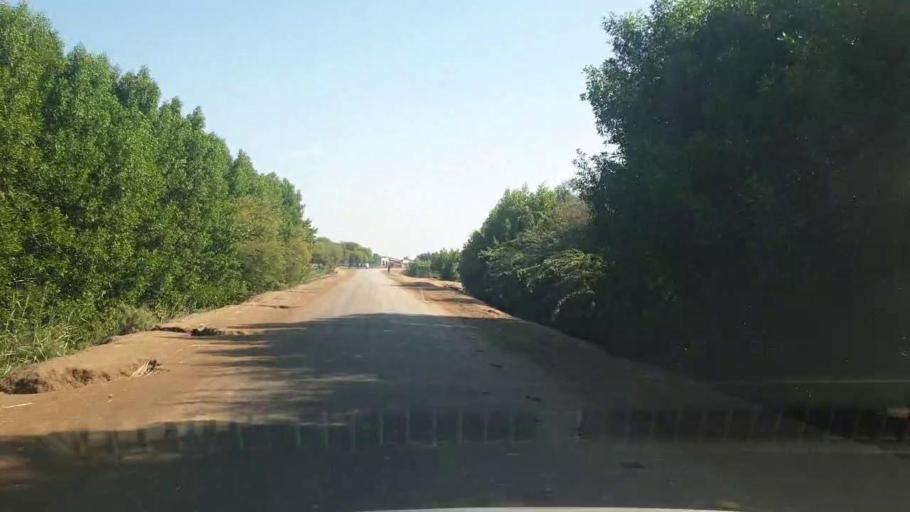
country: PK
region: Sindh
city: Rajo Khanani
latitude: 24.9197
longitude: 68.9263
